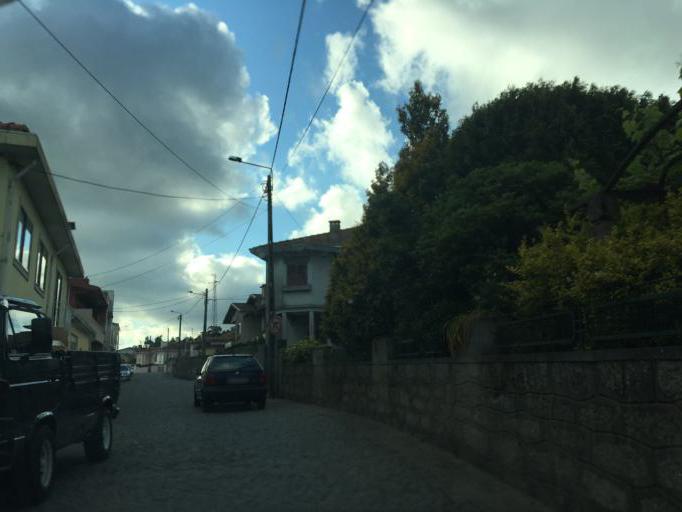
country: PT
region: Porto
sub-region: Maia
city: Anta
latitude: 41.2843
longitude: -8.6062
